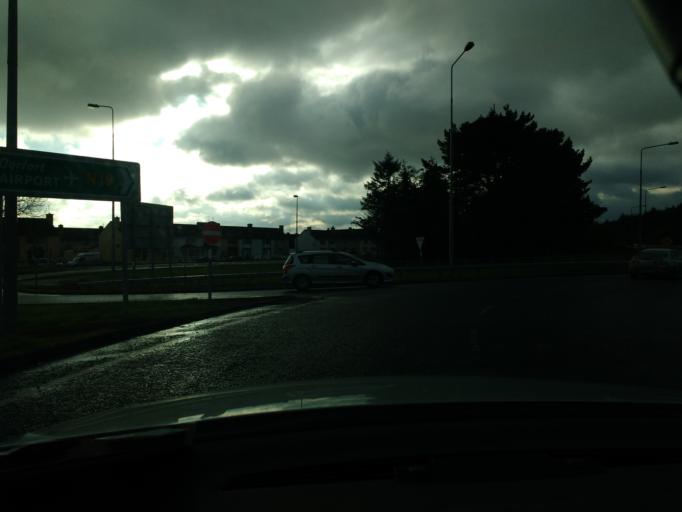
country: IE
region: Munster
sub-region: An Clar
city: Shannon
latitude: 52.7031
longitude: -8.8937
